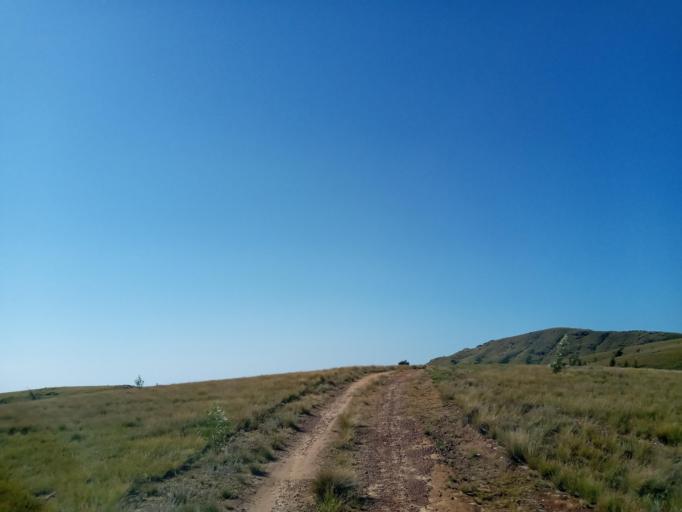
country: MG
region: Anosy
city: Fort Dauphin
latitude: -24.9113
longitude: 47.0710
